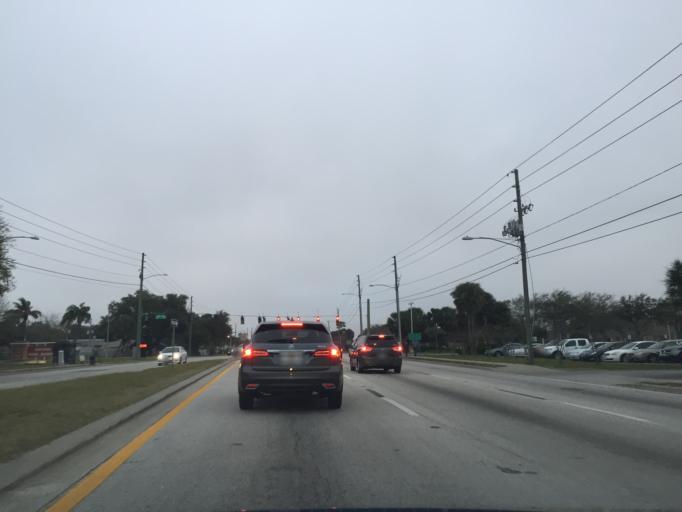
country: US
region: Florida
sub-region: Pinellas County
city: South Highpoint
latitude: 27.9037
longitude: -82.7006
